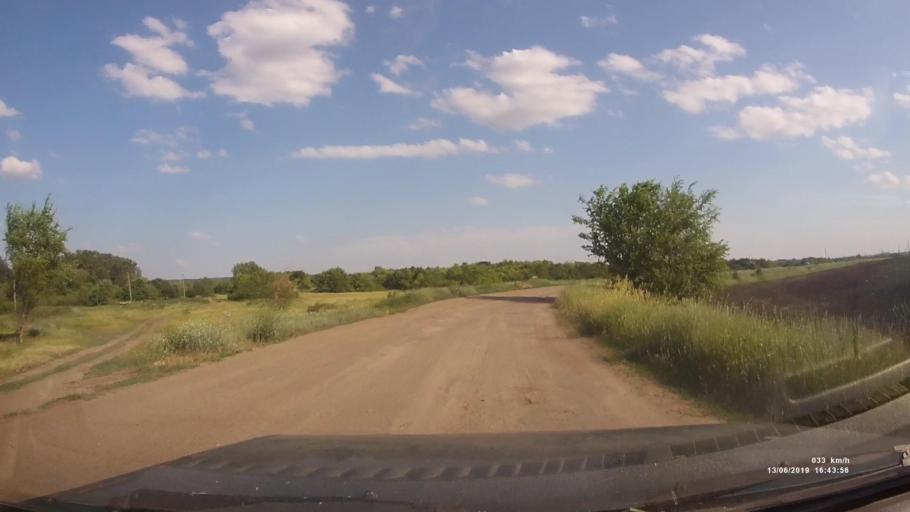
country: RU
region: Rostov
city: Kazanskaya
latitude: 49.9479
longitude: 41.4222
